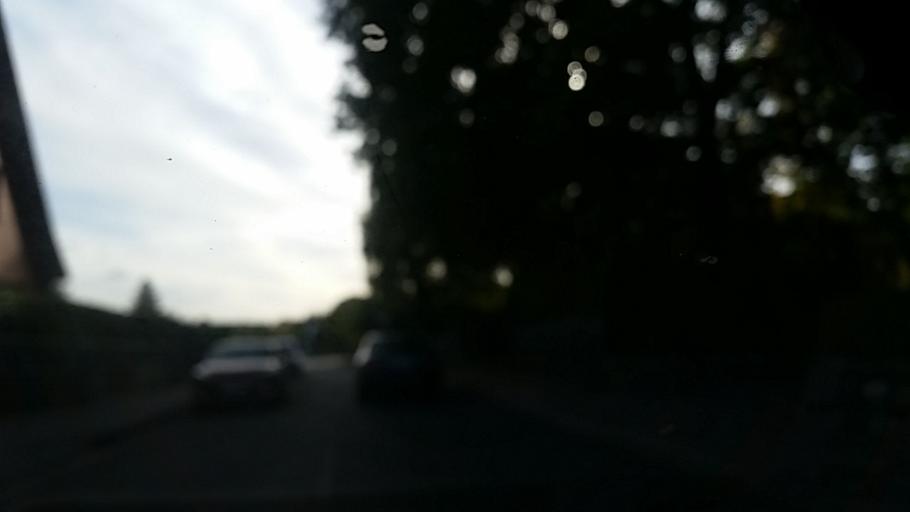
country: DE
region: Schleswig-Holstein
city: Kayhude
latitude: 53.7356
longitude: 10.1531
